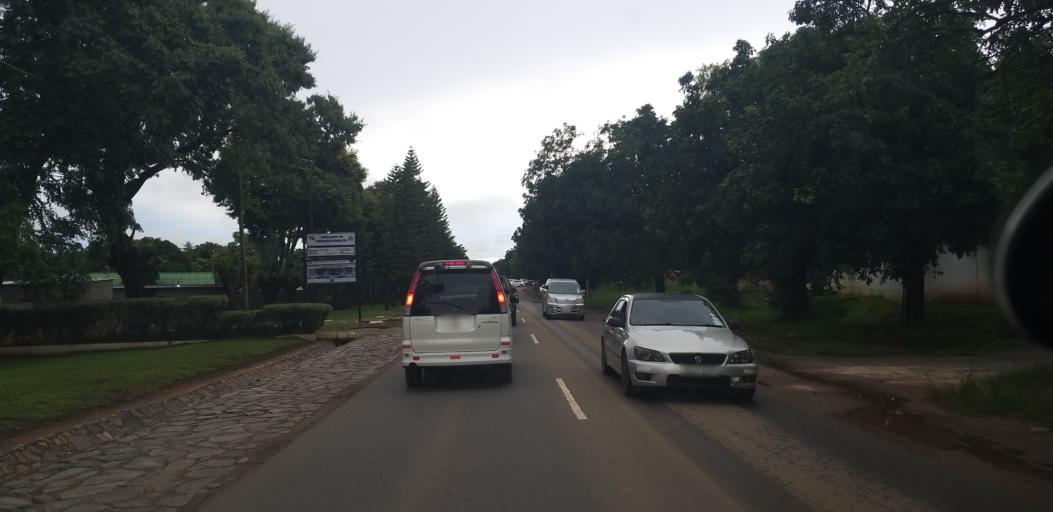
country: ZM
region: Lusaka
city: Lusaka
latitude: -15.4286
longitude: 28.3408
